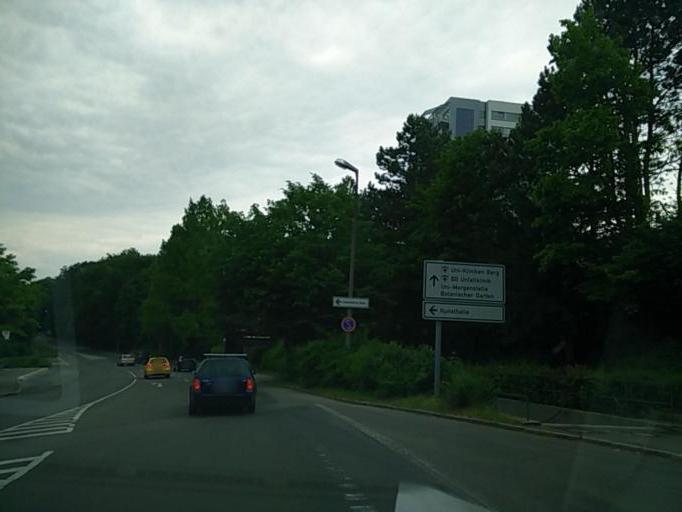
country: DE
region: Baden-Wuerttemberg
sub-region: Tuebingen Region
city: Tuebingen
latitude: 48.5439
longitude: 9.0469
